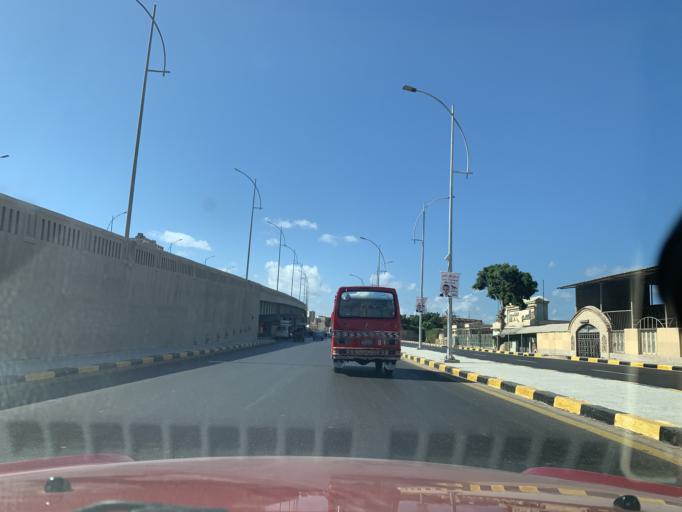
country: EG
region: Alexandria
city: Alexandria
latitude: 31.2232
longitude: 29.9860
